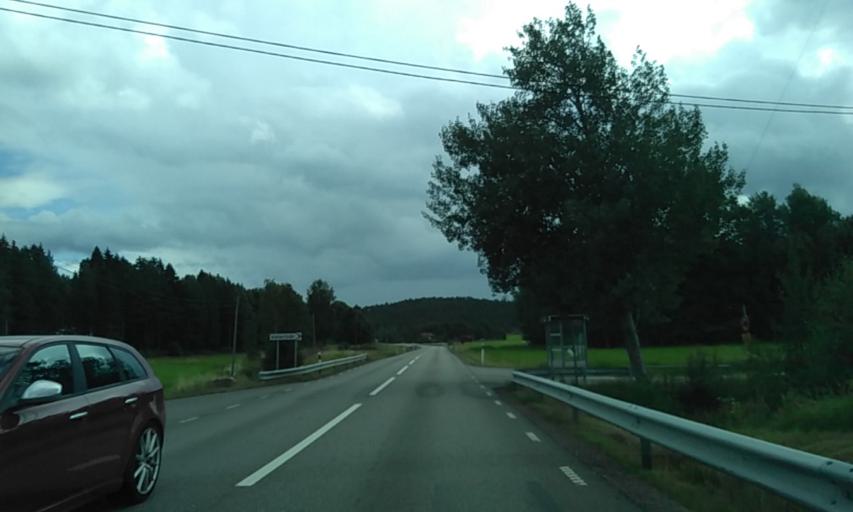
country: SE
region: Vaestra Goetaland
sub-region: Alingsas Kommun
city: Alingsas
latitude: 57.9550
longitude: 12.4586
